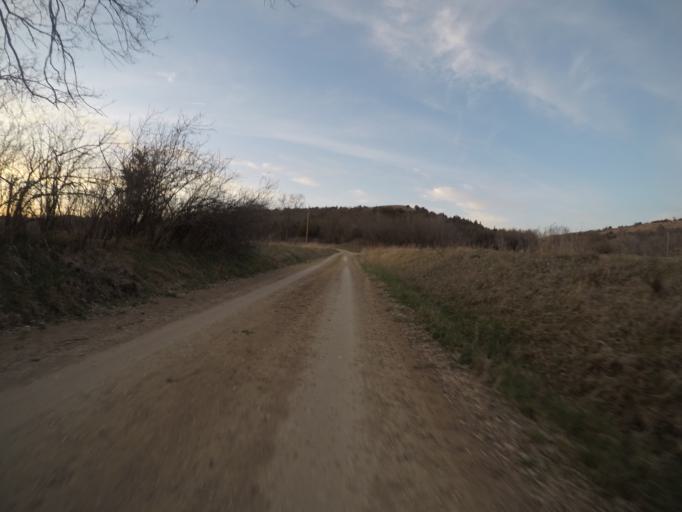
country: US
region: Kansas
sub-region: Riley County
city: Ogden
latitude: 39.1670
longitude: -96.6679
